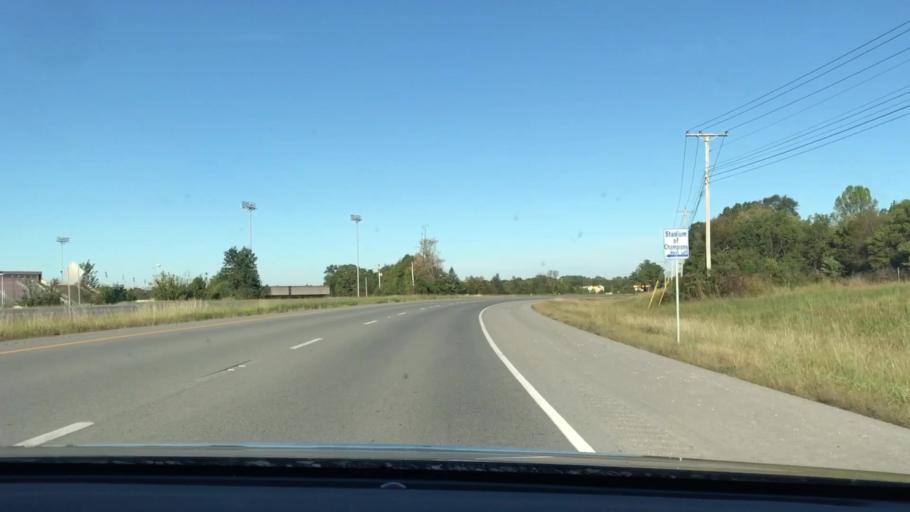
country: US
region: Kentucky
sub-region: Christian County
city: Hopkinsville
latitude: 36.8181
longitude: -87.4984
